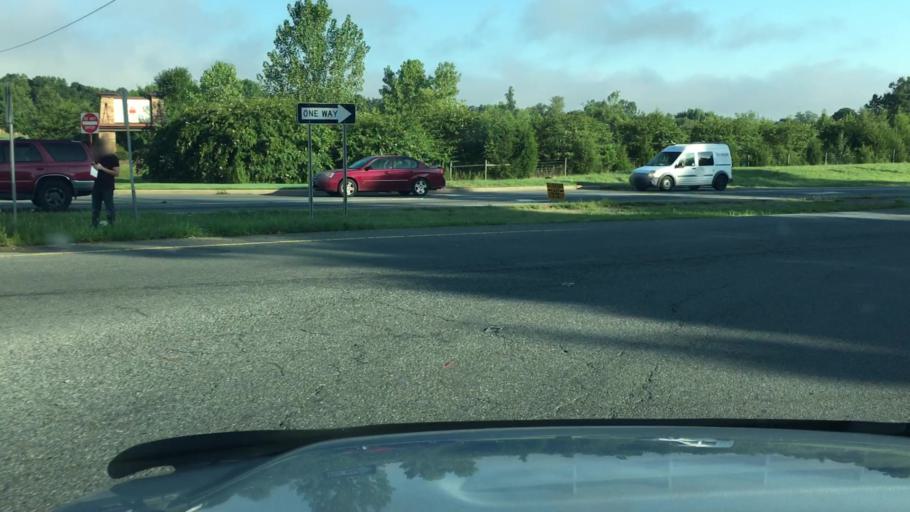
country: US
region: North Carolina
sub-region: Gaston County
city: Mount Holly
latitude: 35.2898
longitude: -80.9664
